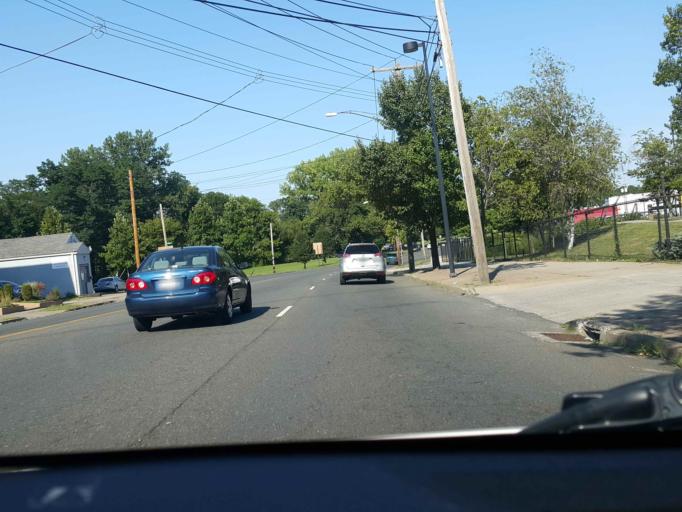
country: US
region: Connecticut
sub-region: New Haven County
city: West Haven
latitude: 41.2966
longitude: -72.9551
